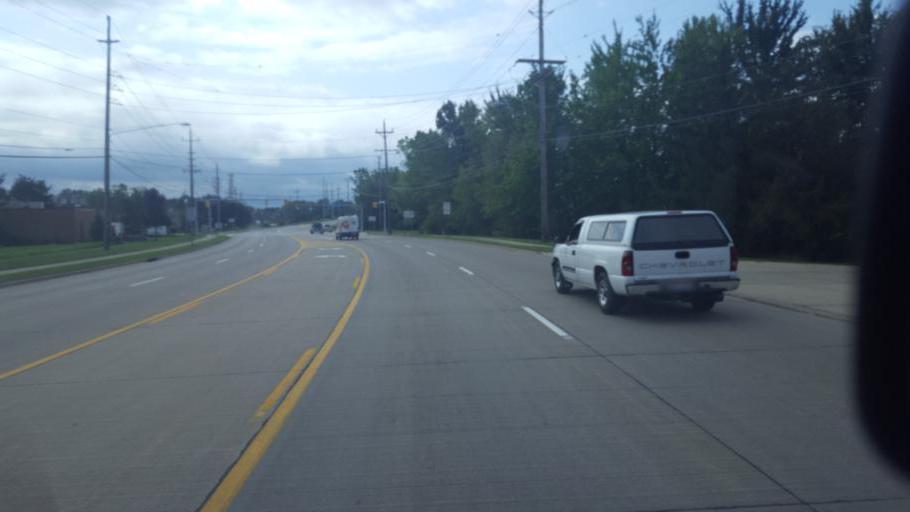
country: US
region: Ohio
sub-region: Lake County
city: Mentor
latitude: 41.7023
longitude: -81.3080
